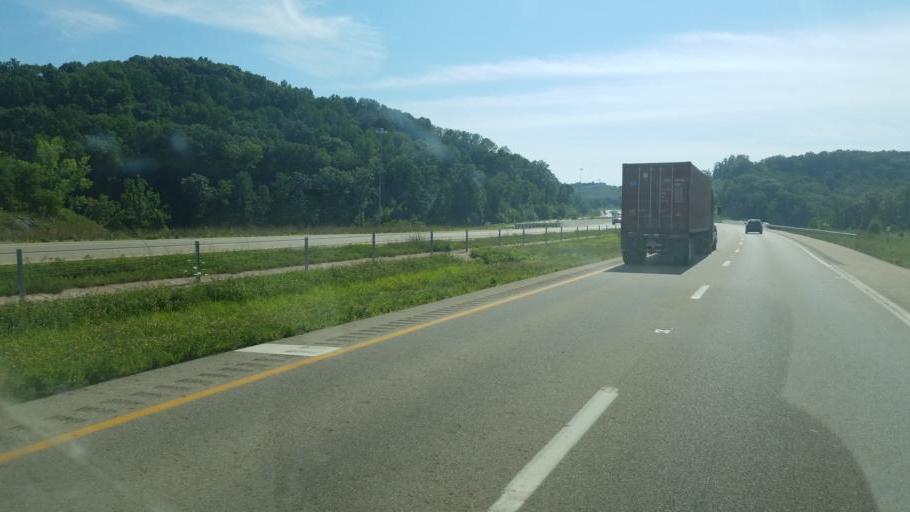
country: US
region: Ohio
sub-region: Athens County
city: Nelsonville
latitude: 39.4723
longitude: -82.2503
